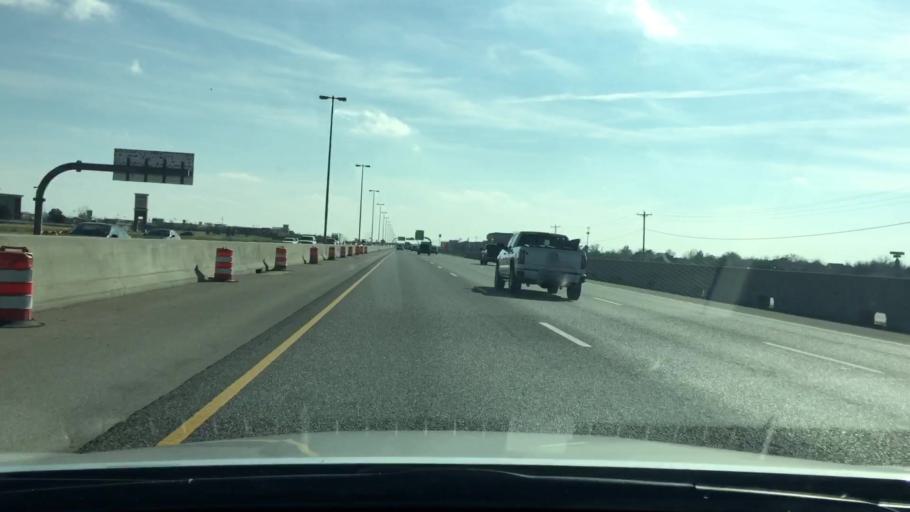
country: US
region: Oklahoma
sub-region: Cleveland County
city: Norman
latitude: 35.2456
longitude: -97.4856
